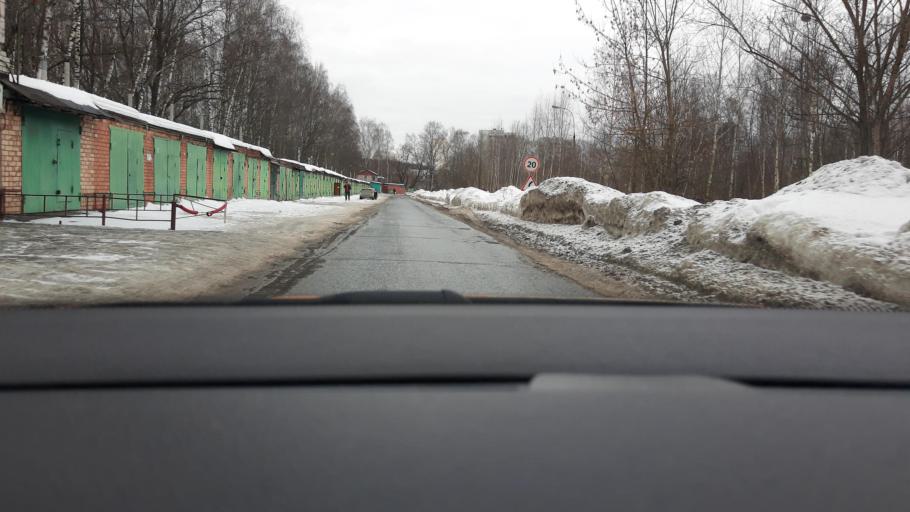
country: RU
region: Moscow
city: Babushkin
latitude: 55.8490
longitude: 37.7038
